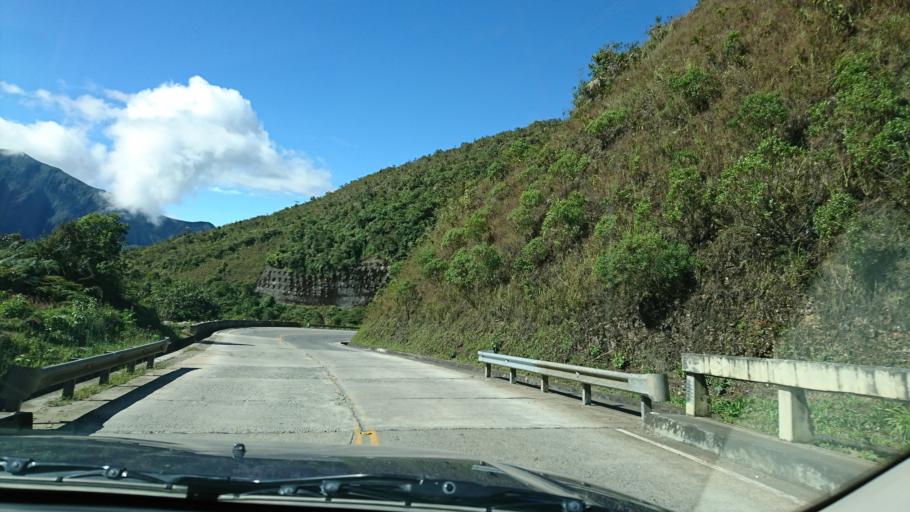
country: BO
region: La Paz
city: Coroico
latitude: -16.2153
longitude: -67.8097
